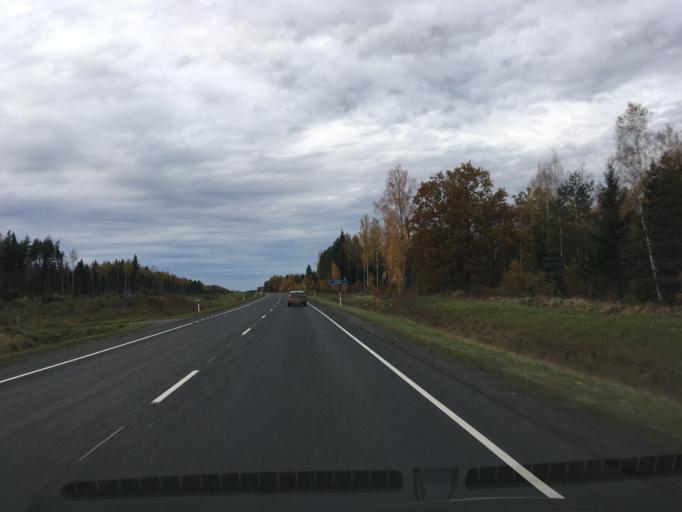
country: EE
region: Harju
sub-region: Nissi vald
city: Turba
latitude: 58.9501
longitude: 24.0827
